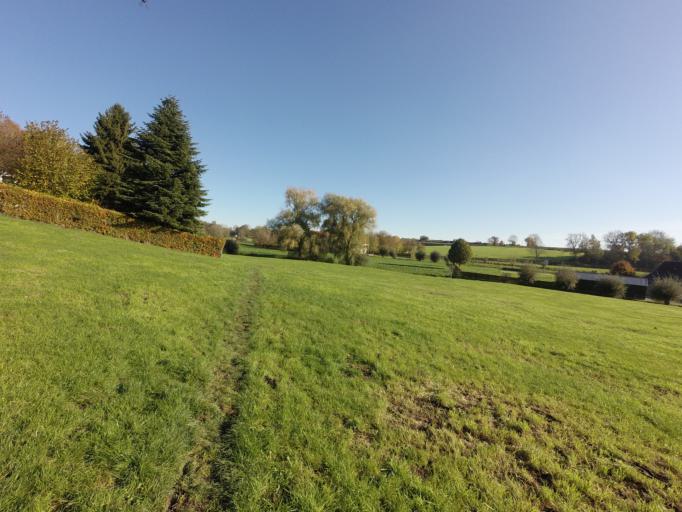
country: NL
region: Limburg
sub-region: Gemeente Simpelveld
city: Simpelveld
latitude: 50.8297
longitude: 5.9622
